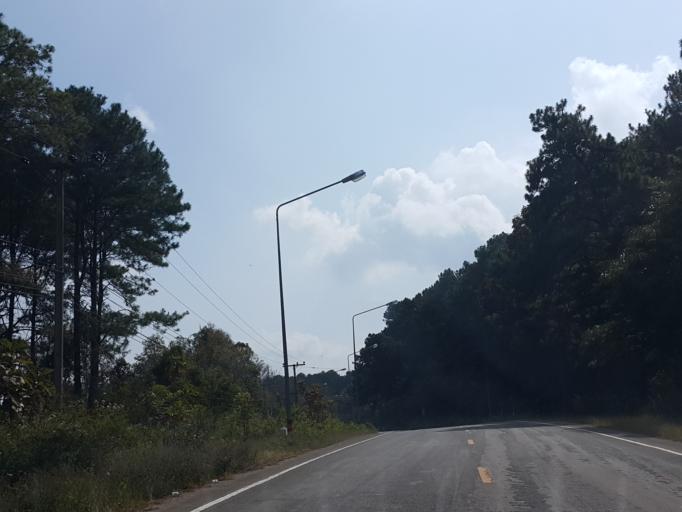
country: TH
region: Chiang Mai
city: Hot
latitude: 18.1333
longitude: 98.3750
